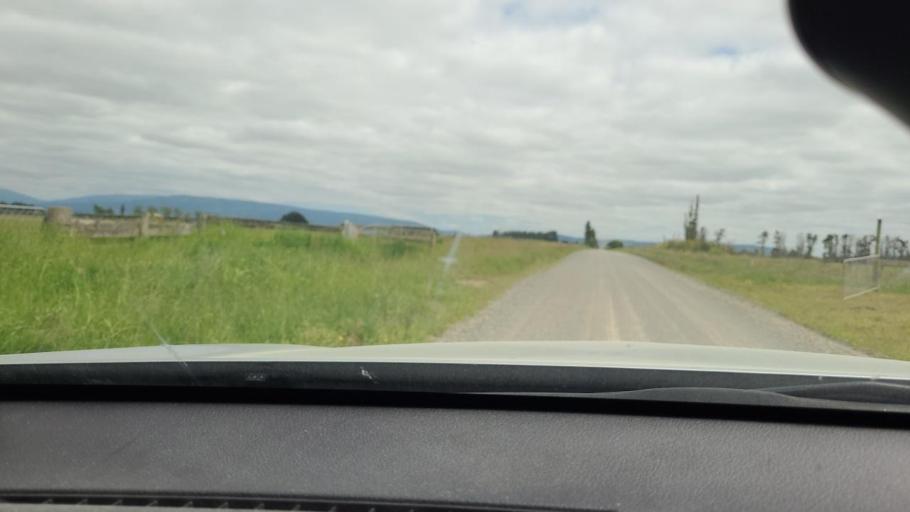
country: NZ
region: Southland
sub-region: Southland District
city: Riverton
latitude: -46.0658
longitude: 168.0473
